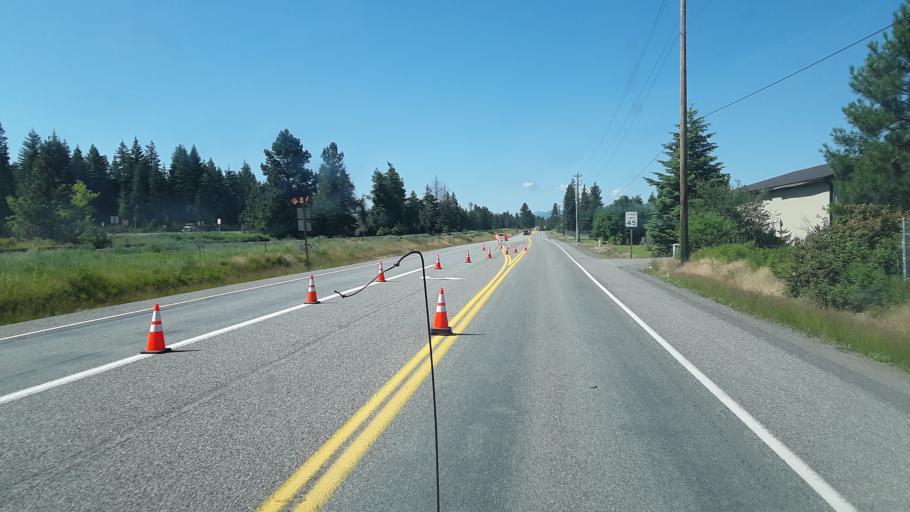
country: US
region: Idaho
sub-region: Kootenai County
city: Hayden
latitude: 47.8310
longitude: -116.7798
